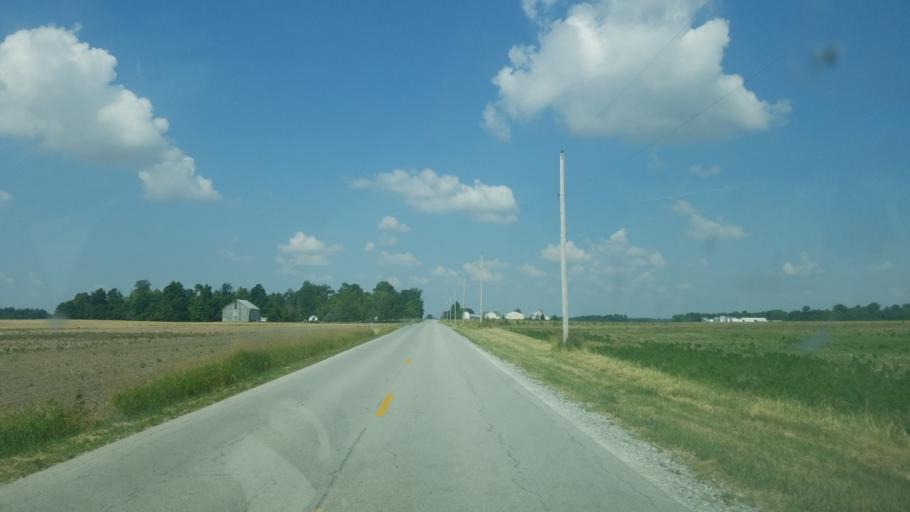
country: US
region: Ohio
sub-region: Auglaize County
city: Wapakoneta
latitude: 40.5704
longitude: -84.1300
